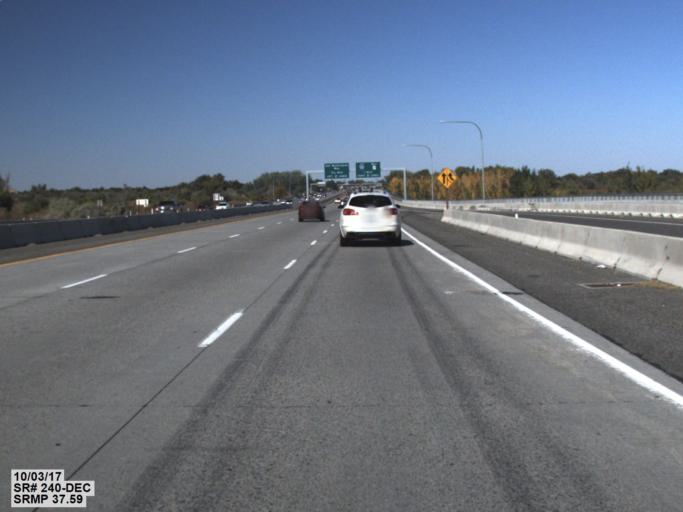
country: US
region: Washington
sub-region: Benton County
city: Richland
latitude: 46.2406
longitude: -119.2454
